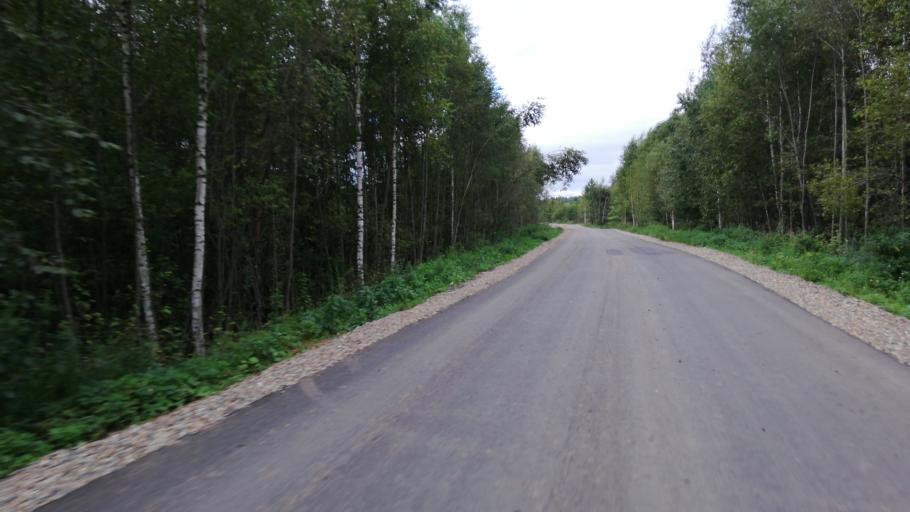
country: RU
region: Jaroslavl
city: Konstantinovskiy
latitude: 57.8054
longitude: 39.7189
